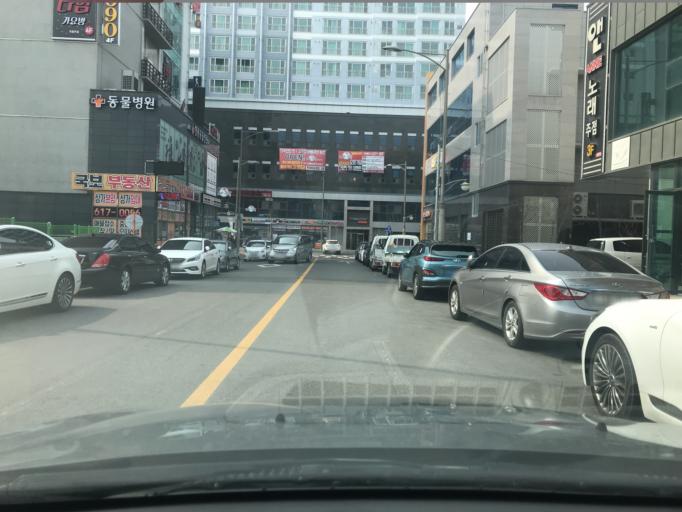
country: KR
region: Daegu
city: Hwawon
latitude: 35.6923
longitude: 128.4593
